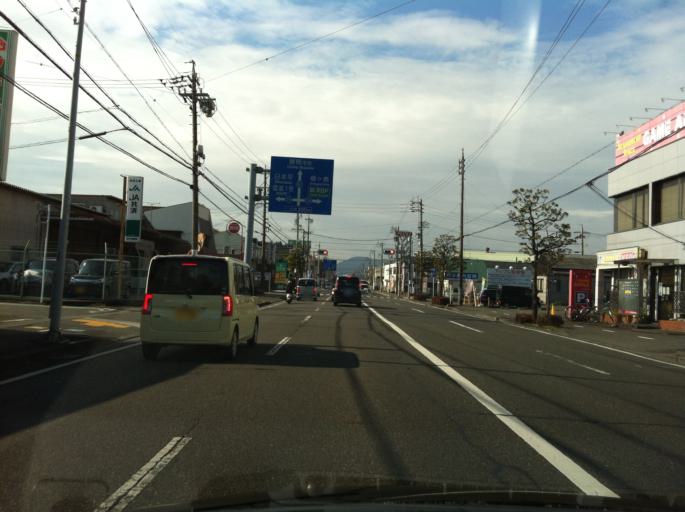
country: JP
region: Shizuoka
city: Shizuoka-shi
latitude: 34.9993
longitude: 138.4165
